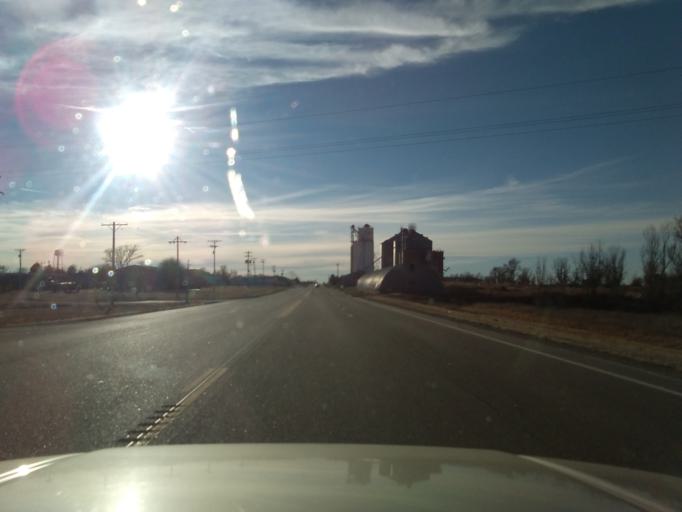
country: US
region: Kansas
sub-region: Sheridan County
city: Hoxie
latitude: 39.5461
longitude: -100.5630
